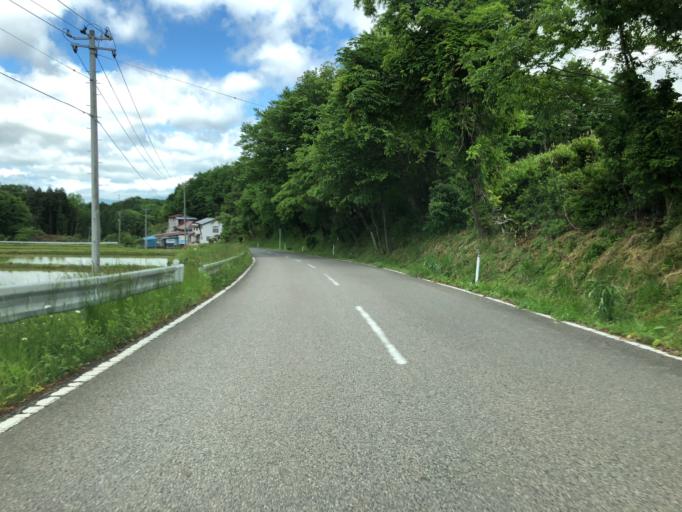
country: JP
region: Fukushima
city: Miharu
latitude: 37.4696
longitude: 140.4650
